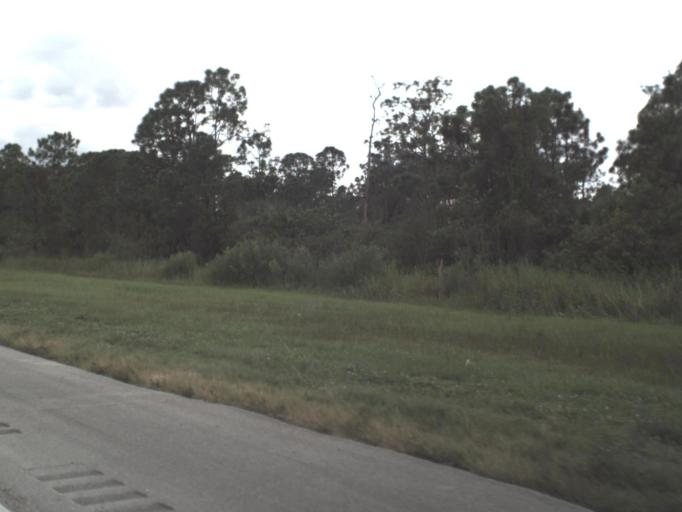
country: US
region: Florida
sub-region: Martin County
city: Palm City
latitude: 27.1244
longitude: -80.2796
